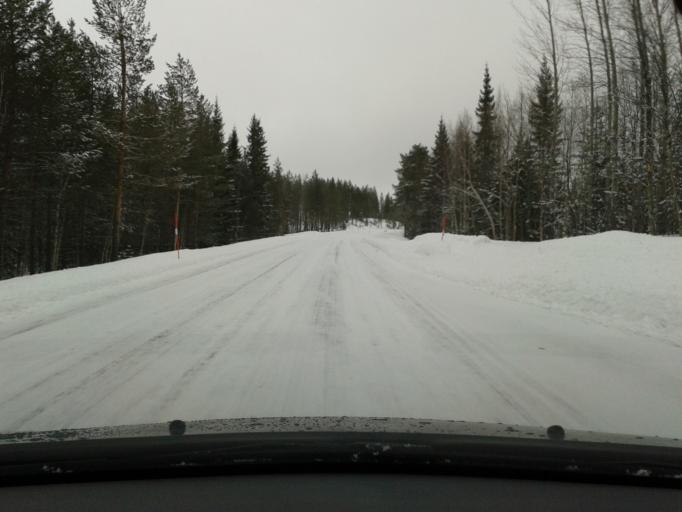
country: SE
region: Vaesterbotten
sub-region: Vilhelmina Kommun
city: Sjoberg
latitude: 64.8701
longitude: 15.8909
